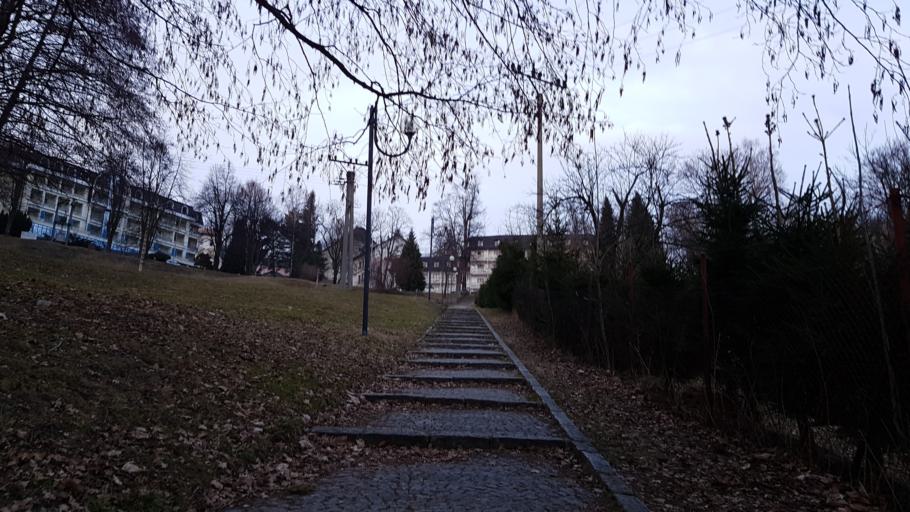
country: CZ
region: Olomoucky
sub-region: Okres Jesenik
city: Jesenik
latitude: 50.2385
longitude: 17.1866
